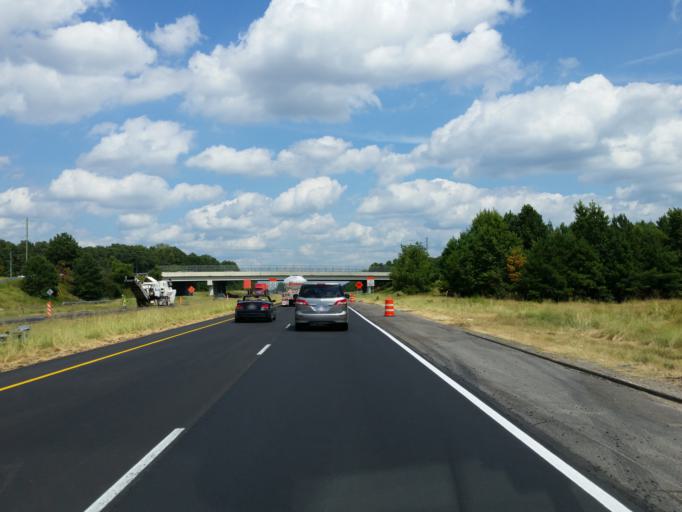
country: US
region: Georgia
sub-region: Gwinnett County
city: Lawrenceville
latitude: 33.9608
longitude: -84.0635
